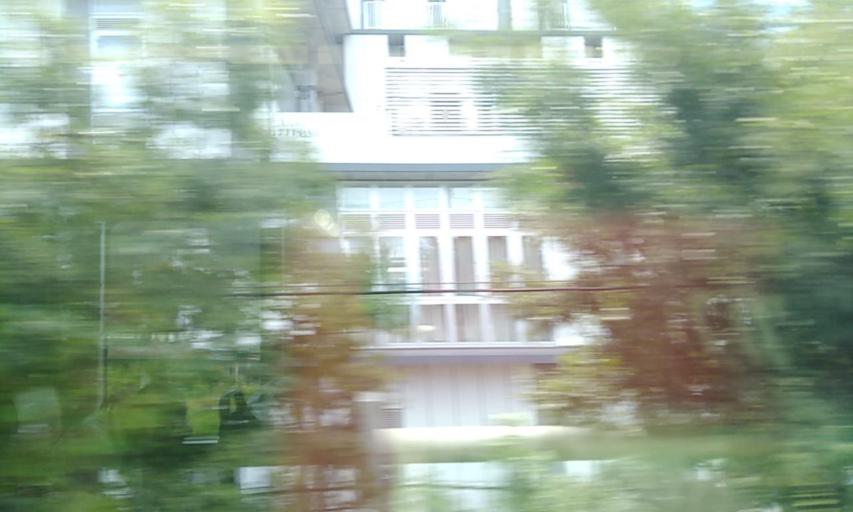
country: JP
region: Kagawa
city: Takamatsu-shi
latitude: 34.3462
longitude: 134.0219
